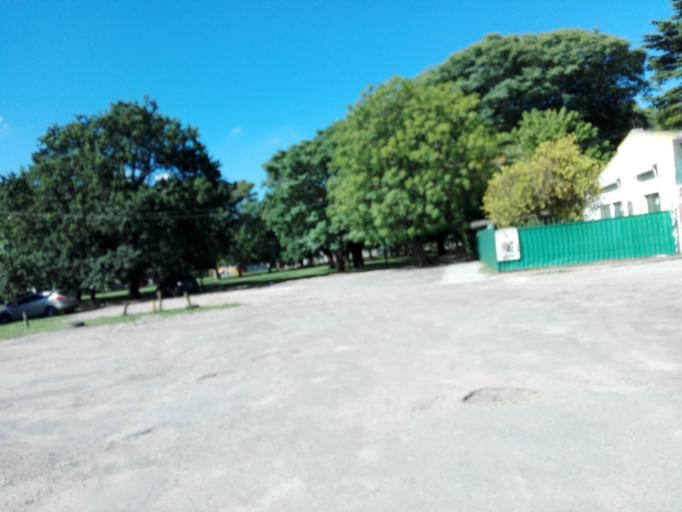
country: AR
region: Buenos Aires
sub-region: Partido de La Plata
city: La Plata
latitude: -34.9318
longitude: -57.9669
